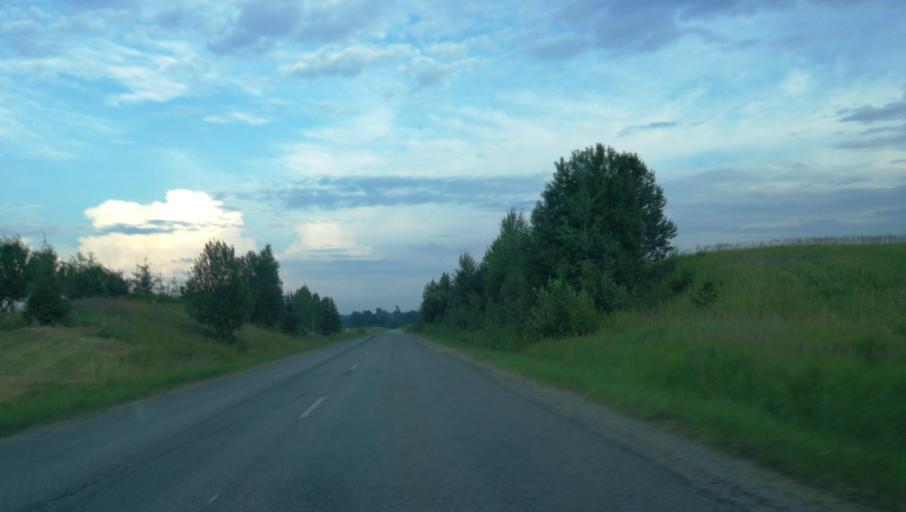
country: LV
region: Cesu Rajons
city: Cesis
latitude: 57.2824
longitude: 25.3146
